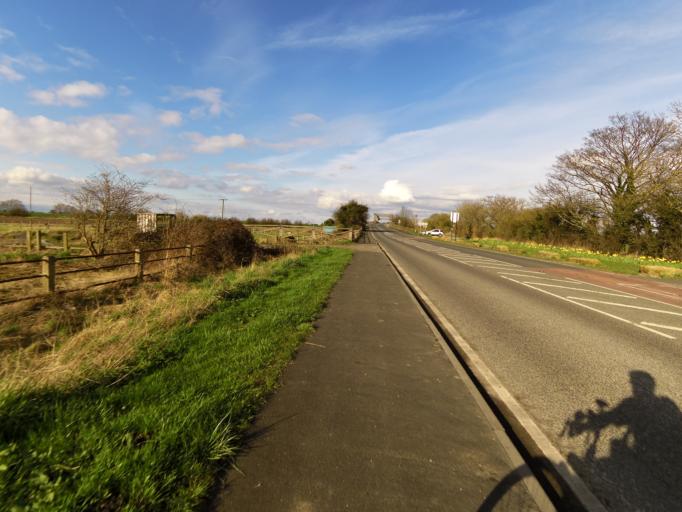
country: GB
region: England
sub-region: East Riding of Yorkshire
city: Snaith
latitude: 53.6948
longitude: -1.0283
